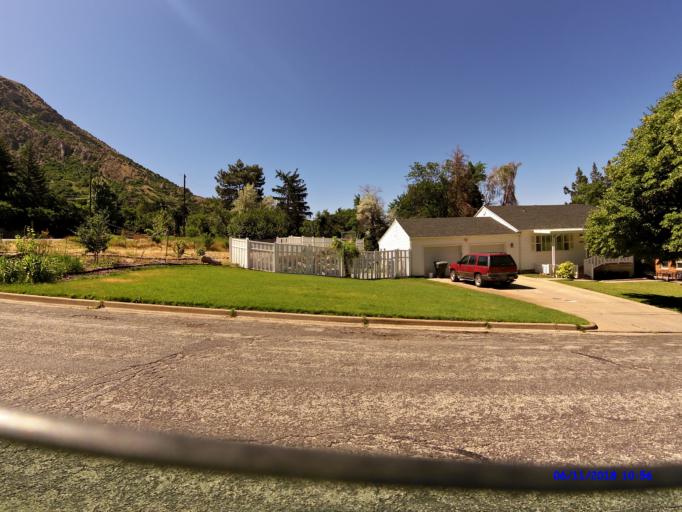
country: US
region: Utah
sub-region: Weber County
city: Ogden
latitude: 41.2160
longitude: -111.9321
